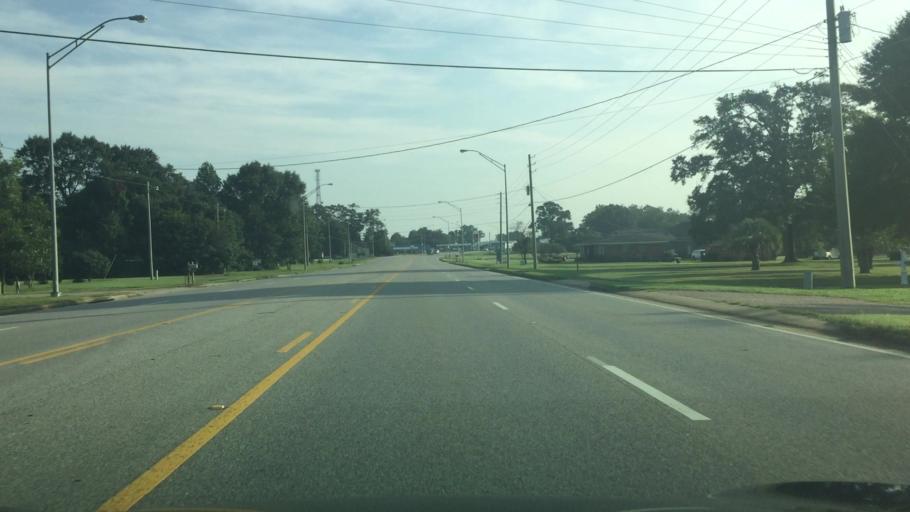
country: US
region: Alabama
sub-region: Covington County
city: Andalusia
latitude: 31.2886
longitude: -86.5036
